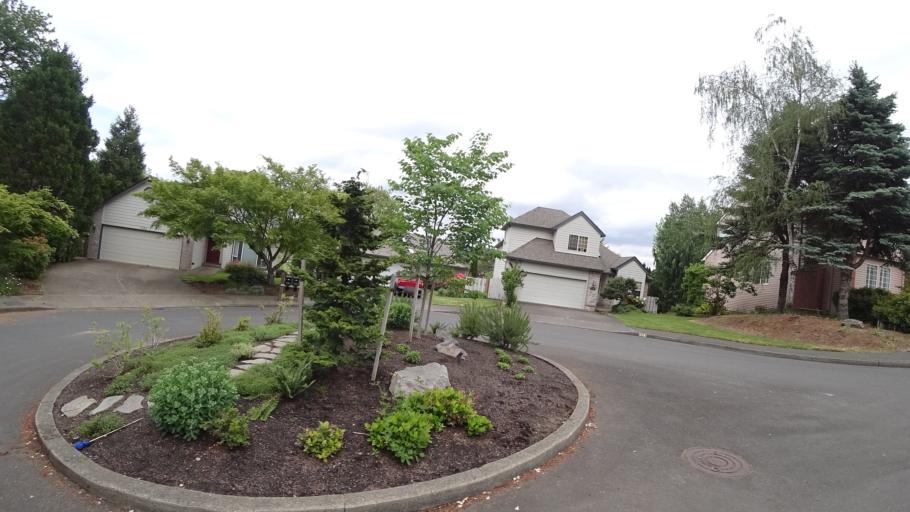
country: US
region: Oregon
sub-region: Washington County
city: Raleigh Hills
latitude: 45.4749
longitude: -122.7535
